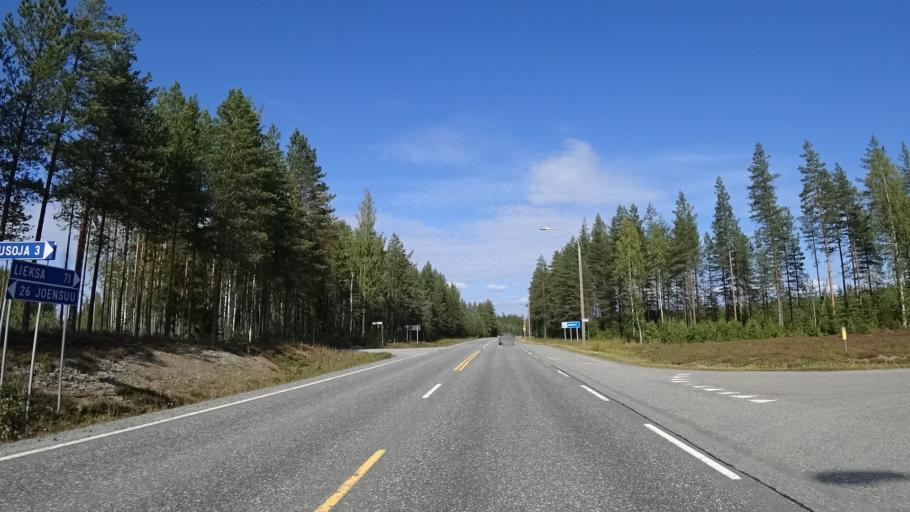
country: FI
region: North Karelia
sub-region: Joensuu
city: Eno
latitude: 62.7716
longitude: 30.0496
